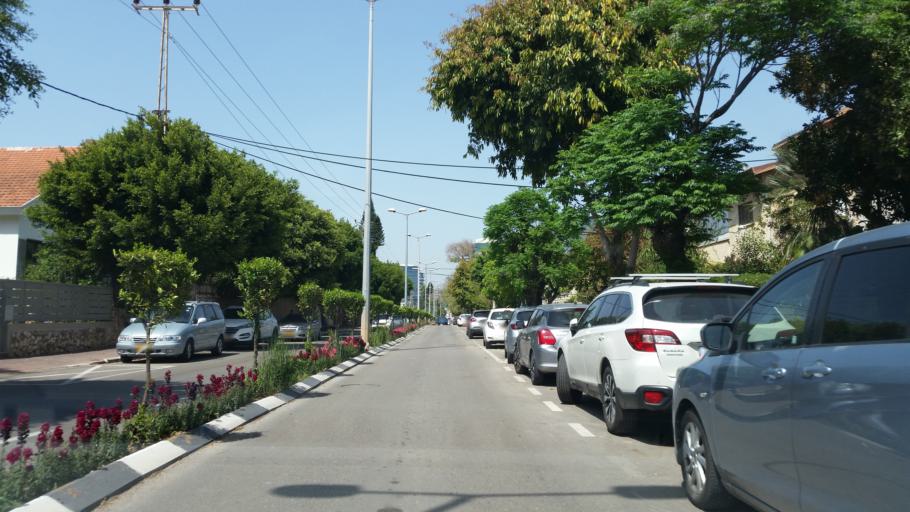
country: IL
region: Central District
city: Ra'anana
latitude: 32.1863
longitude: 34.8827
